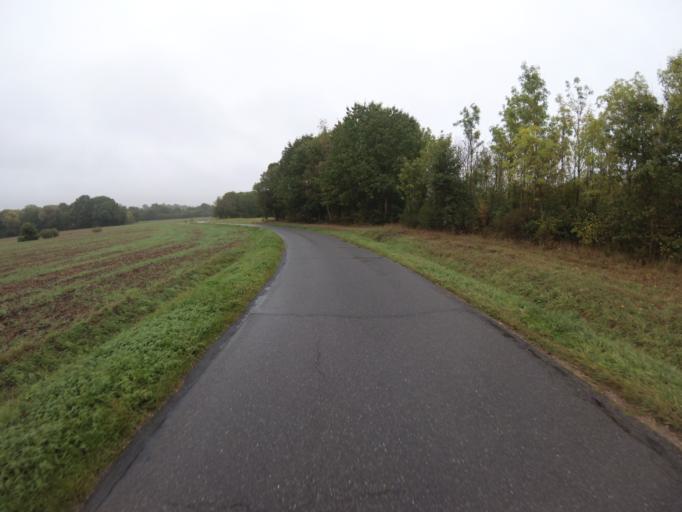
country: FR
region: Ile-de-France
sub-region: Departement de Seine-et-Marne
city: Ferrieres-en-Brie
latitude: 48.8260
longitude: 2.6897
